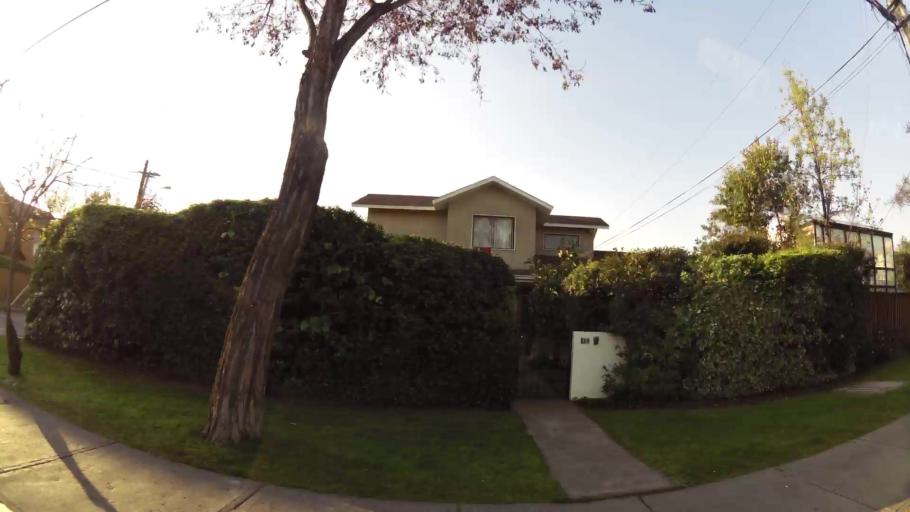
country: CL
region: Santiago Metropolitan
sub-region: Provincia de Santiago
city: Villa Presidente Frei, Nunoa, Santiago, Chile
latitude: -33.3998
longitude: -70.5574
